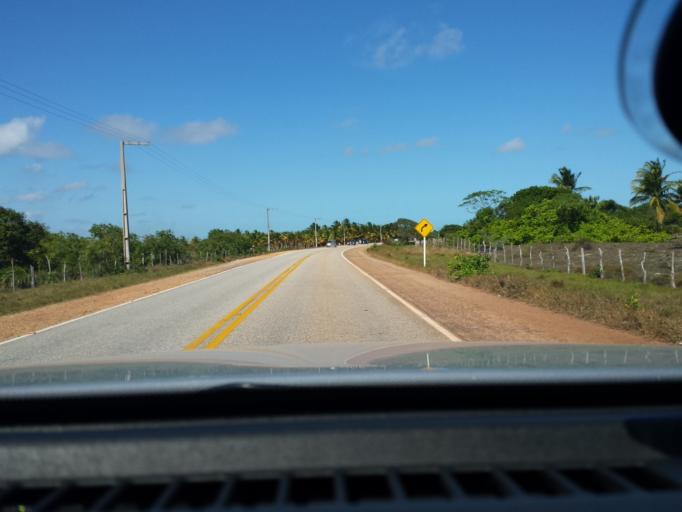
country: BR
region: Sergipe
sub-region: Estancia
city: Estancia
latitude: -11.2640
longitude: -37.2637
